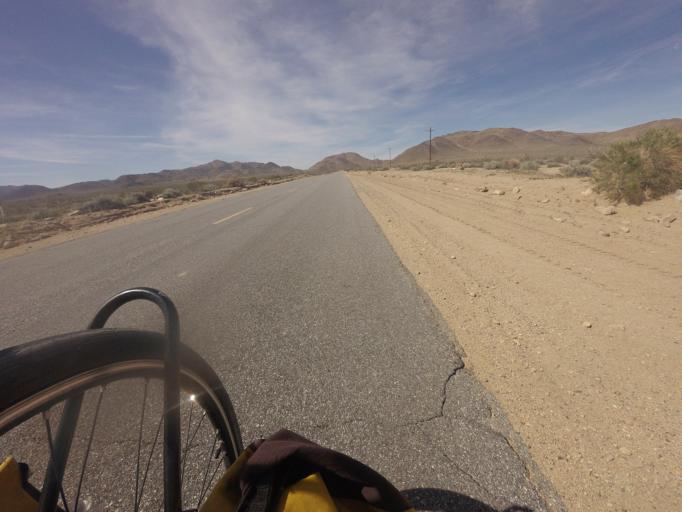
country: US
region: California
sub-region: San Bernardino County
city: Searles Valley
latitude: 35.5707
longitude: -117.4437
